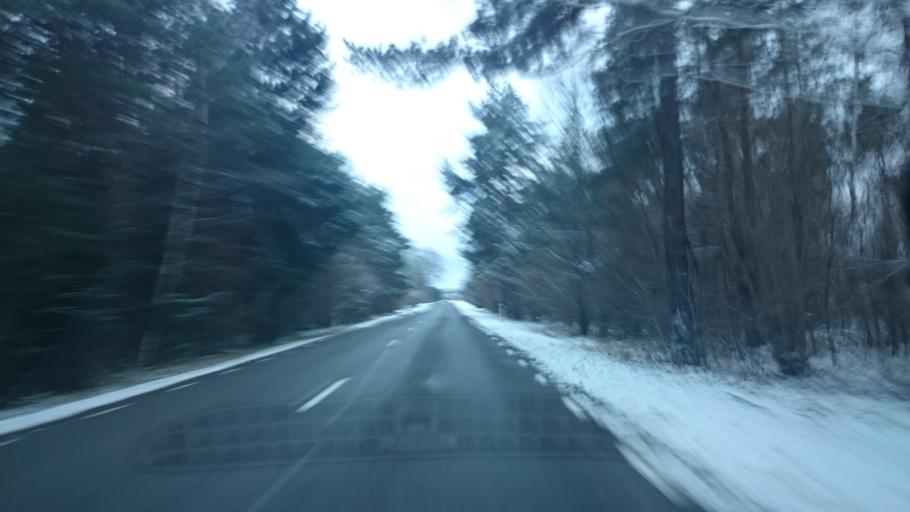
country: EE
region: Saare
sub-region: Kuressaare linn
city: Kuressaare
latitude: 58.3844
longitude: 22.6393
